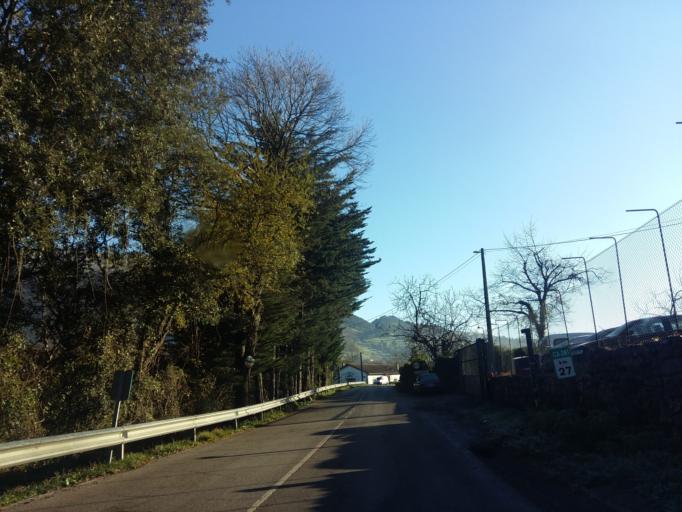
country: ES
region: Cantabria
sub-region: Provincia de Cantabria
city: Arredondo
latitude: 43.2820
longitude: -3.5415
